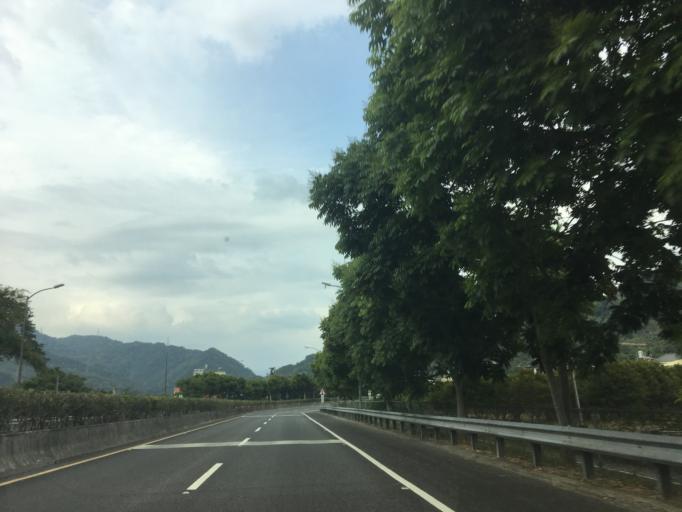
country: TW
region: Taiwan
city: Zhongxing New Village
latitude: 24.0127
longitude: 120.8168
